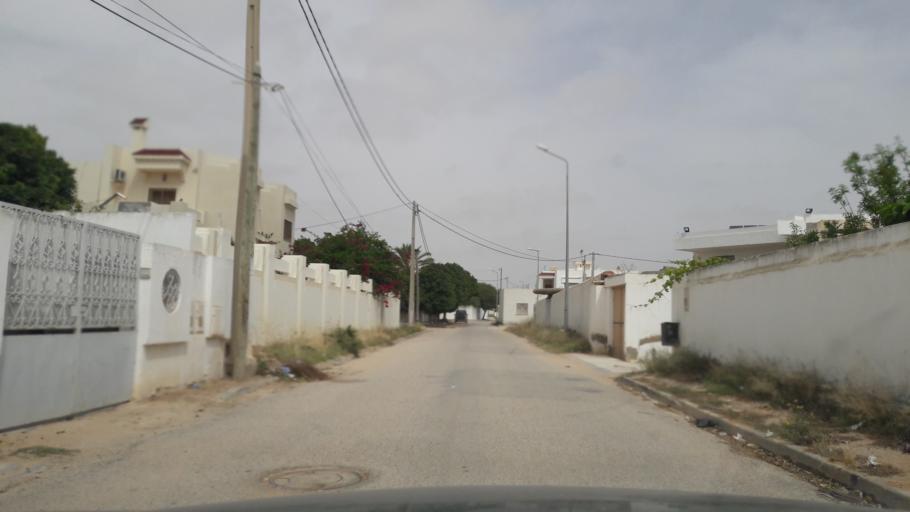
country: TN
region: Safaqis
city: Sfax
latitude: 34.7751
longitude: 10.7579
